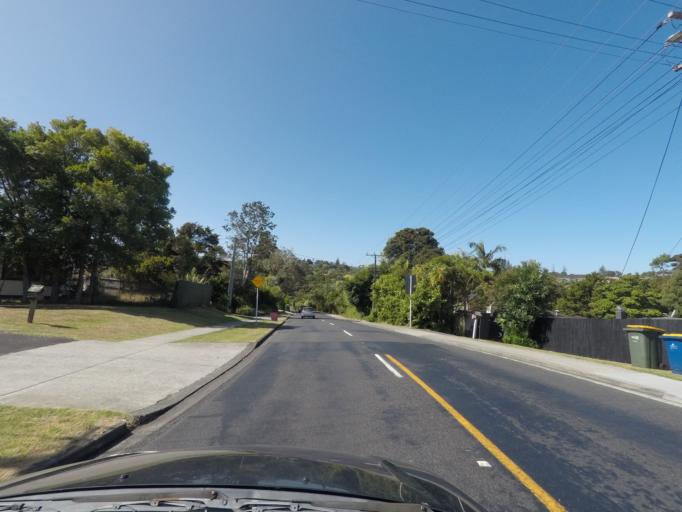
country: NZ
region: Auckland
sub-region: Auckland
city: Waitakere
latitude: -36.9259
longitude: 174.6551
